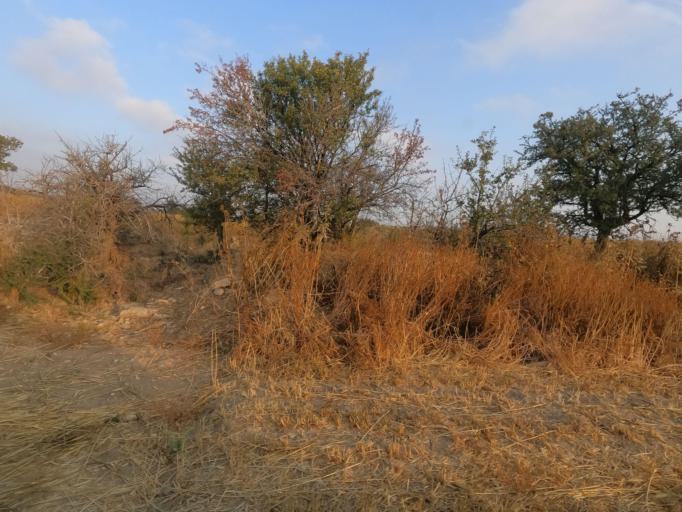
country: CY
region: Larnaka
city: Tersefanou
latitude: 34.8327
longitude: 33.5219
